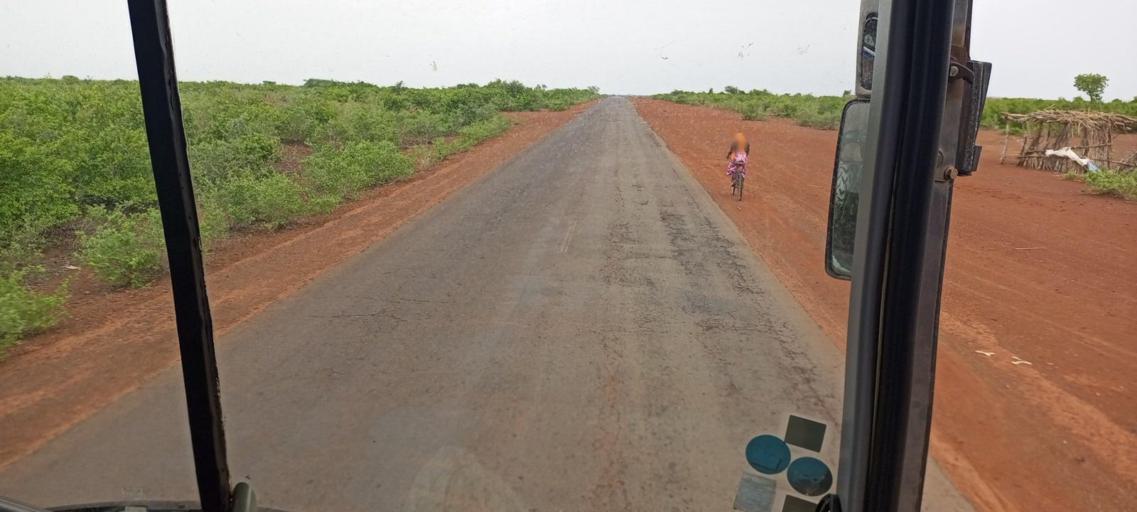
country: ML
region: Segou
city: Bla
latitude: 12.7020
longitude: -5.7240
